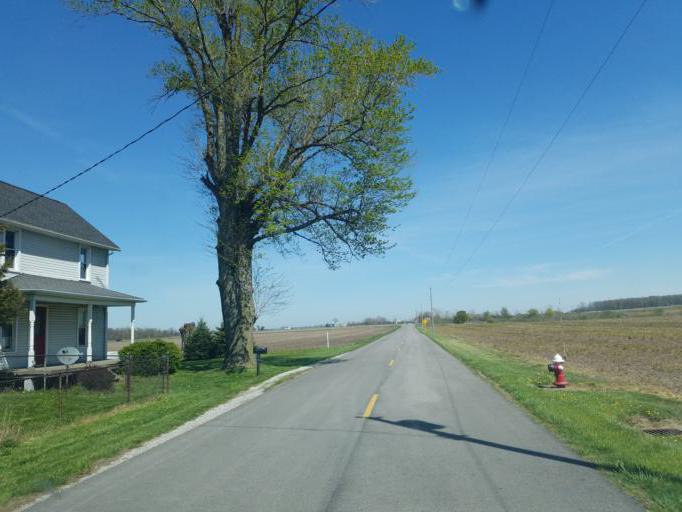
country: US
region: Ohio
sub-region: Huron County
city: Bellevue
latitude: 41.2985
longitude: -82.7841
